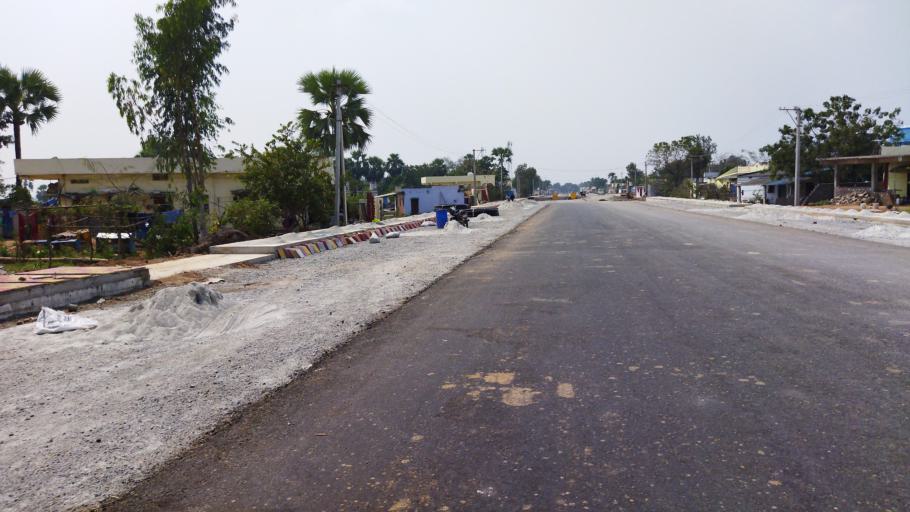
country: IN
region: Telangana
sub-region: Nalgonda
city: Nalgonda
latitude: 17.1466
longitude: 79.3979
